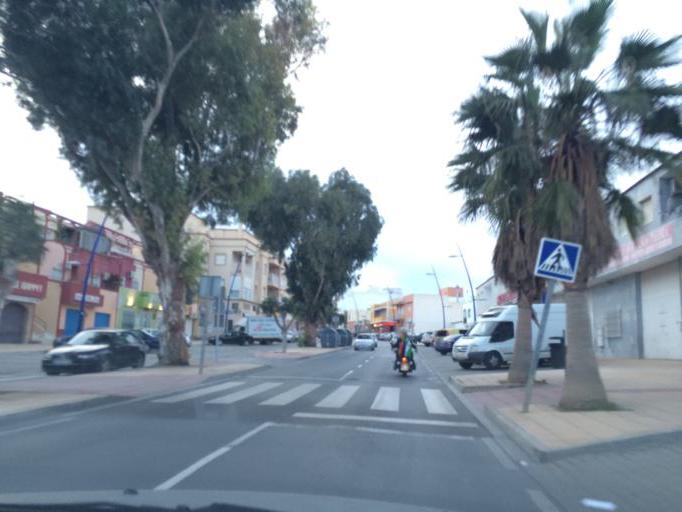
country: ES
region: Andalusia
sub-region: Provincia de Almeria
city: Viator
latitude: 36.8406
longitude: -2.4031
